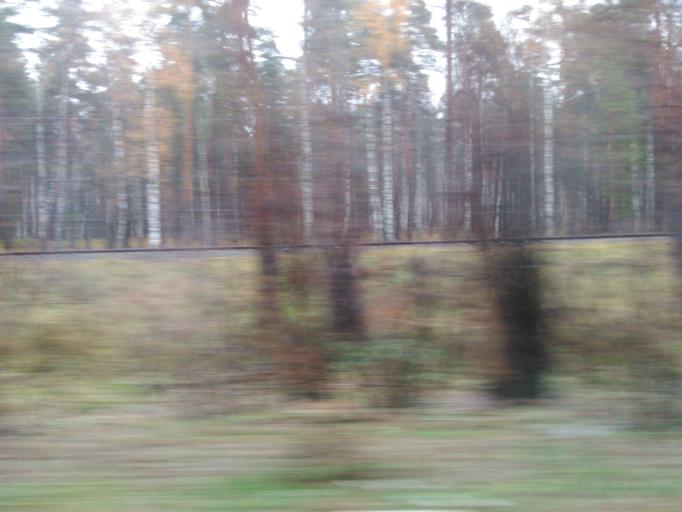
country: RU
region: Tatarstan
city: Osinovo
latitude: 55.8278
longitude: 48.8955
